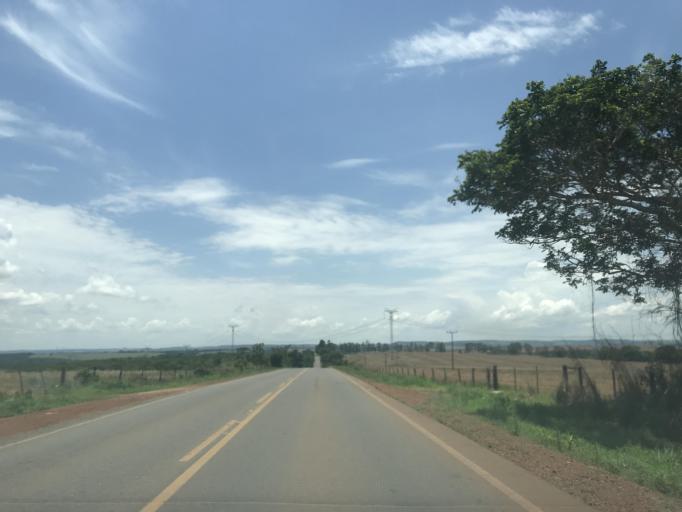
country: BR
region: Goias
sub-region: Vianopolis
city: Vianopolis
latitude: -16.6220
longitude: -48.3535
